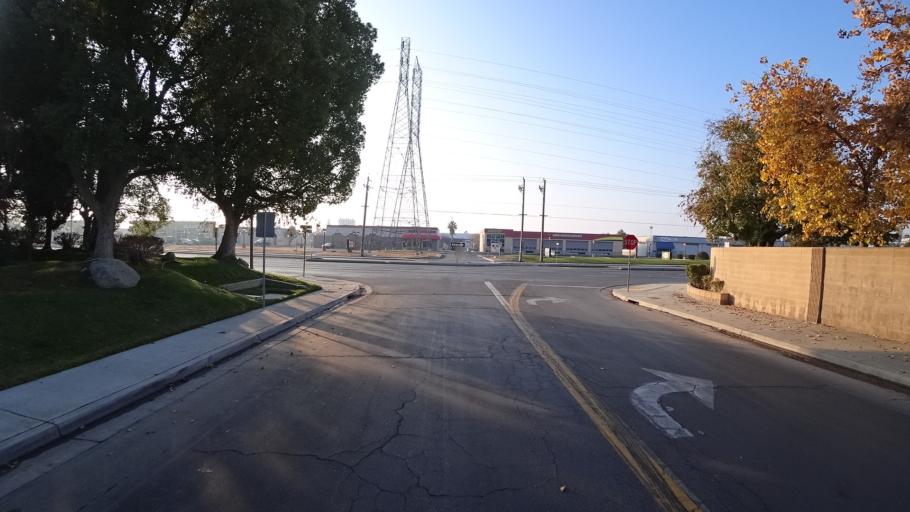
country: US
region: California
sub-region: Kern County
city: Greenacres
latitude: 35.3185
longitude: -119.0799
